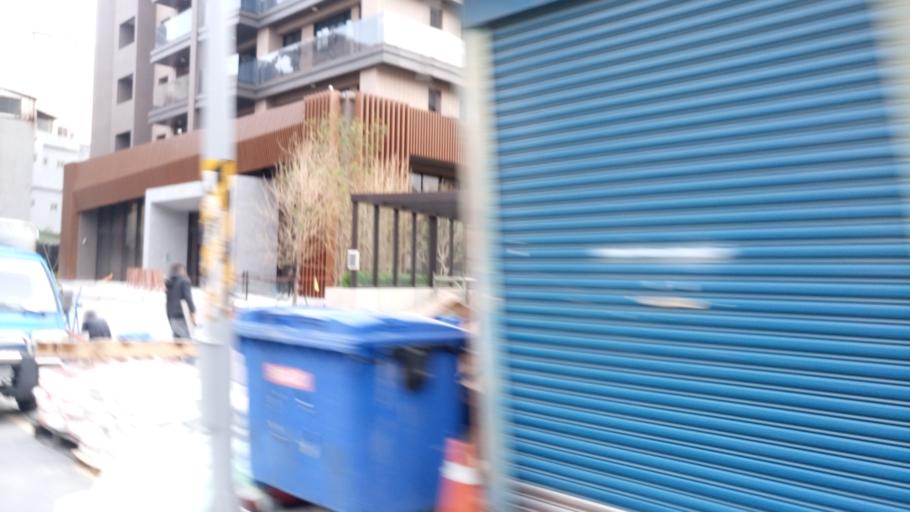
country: TW
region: Taiwan
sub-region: Hsinchu
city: Hsinchu
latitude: 24.8122
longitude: 120.9660
